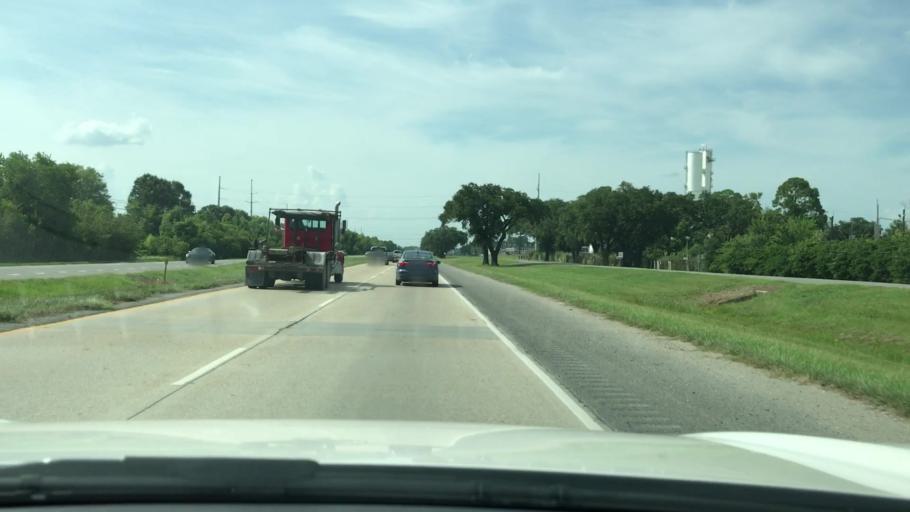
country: US
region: Louisiana
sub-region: Iberville Parish
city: Plaquemine
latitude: 30.3205
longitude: -91.2516
